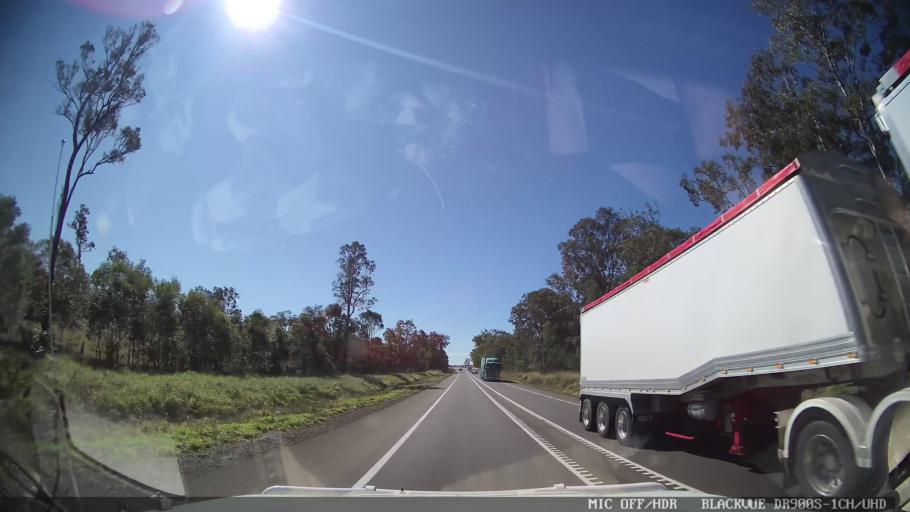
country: AU
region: Queensland
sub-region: Fraser Coast
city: Maryborough
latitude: -25.6502
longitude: 152.6335
